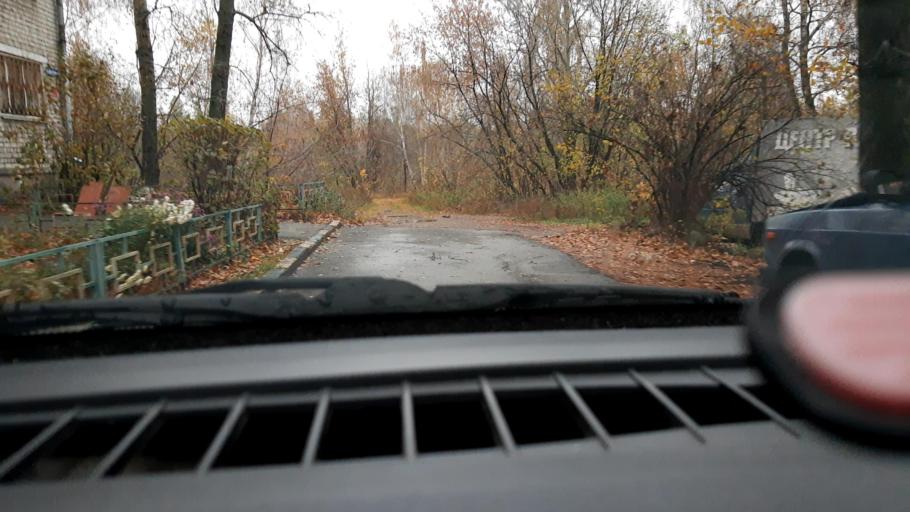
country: RU
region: Nizjnij Novgorod
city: Nizhniy Novgorod
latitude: 56.3028
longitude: 43.9113
